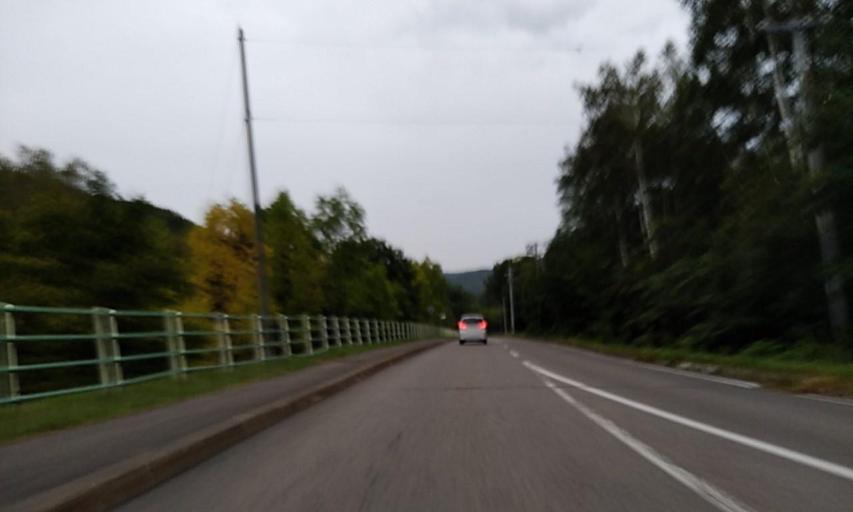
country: JP
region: Hokkaido
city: Abashiri
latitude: 43.9985
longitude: 144.2288
